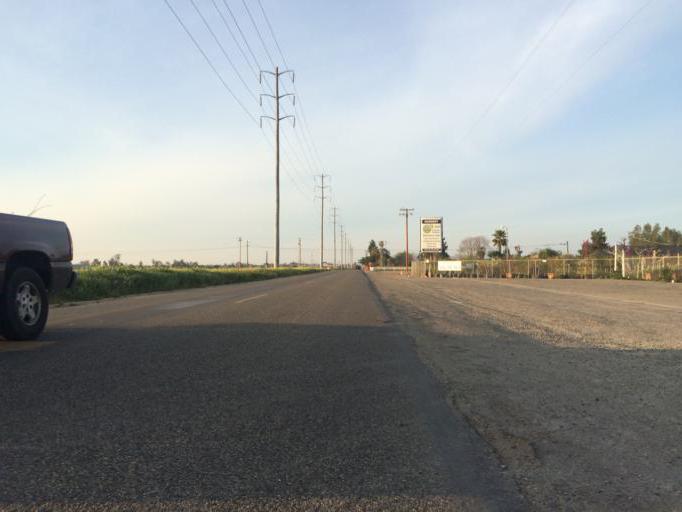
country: US
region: California
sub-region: Fresno County
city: Sunnyside
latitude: 36.7704
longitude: -119.6732
